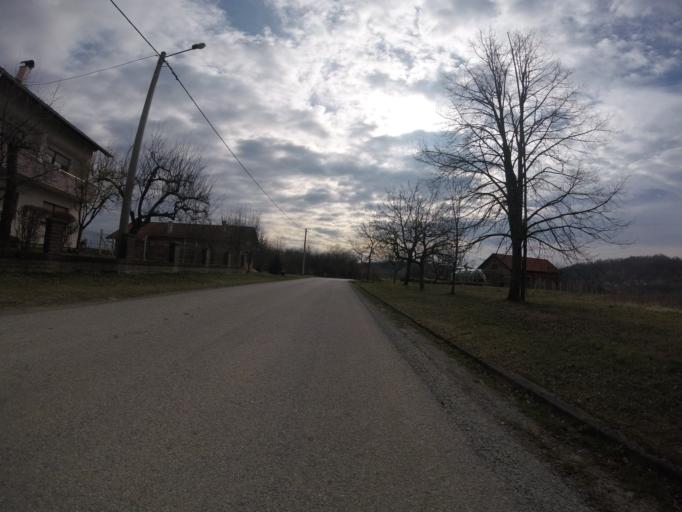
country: HR
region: Sisacko-Moslavacka
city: Glina
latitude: 45.4758
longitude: 16.0241
